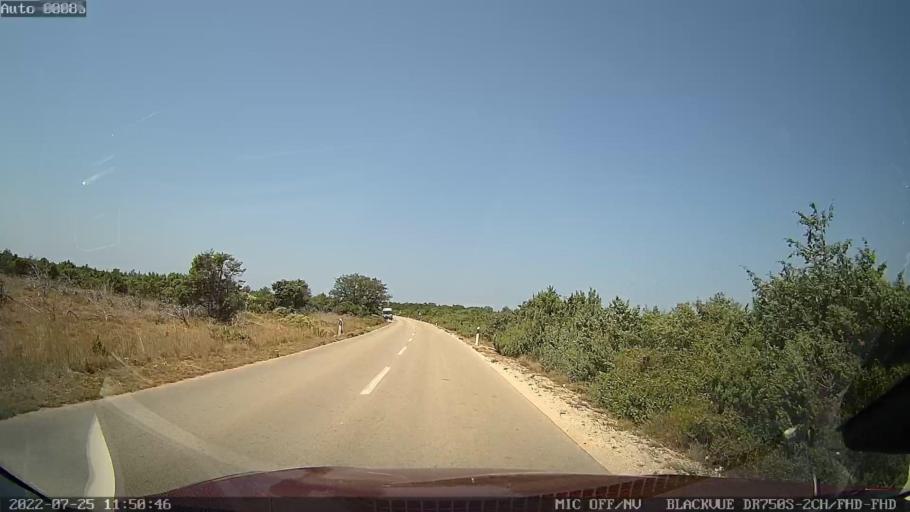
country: HR
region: Zadarska
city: Vrsi
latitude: 44.2375
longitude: 15.2606
